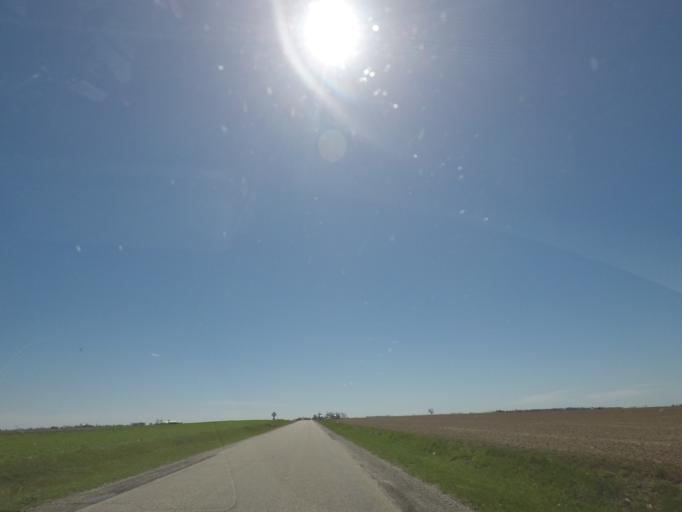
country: US
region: Illinois
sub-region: Logan County
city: Atlanta
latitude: 40.2107
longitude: -89.1944
